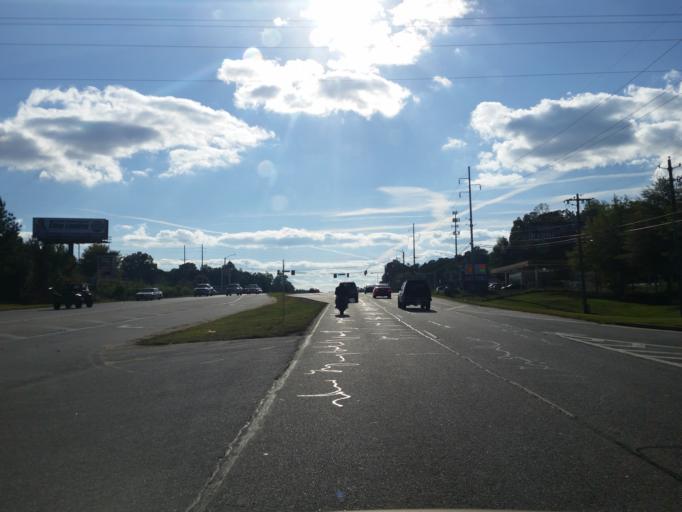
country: US
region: Georgia
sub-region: Paulding County
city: Hiram
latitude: 33.9271
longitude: -84.7459
